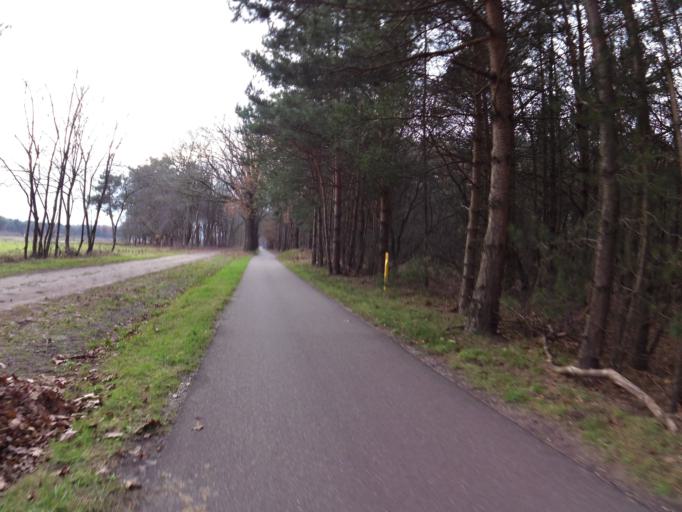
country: NL
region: North Brabant
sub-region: Gemeente Oss
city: Berghem
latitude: 51.7509
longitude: 5.5789
